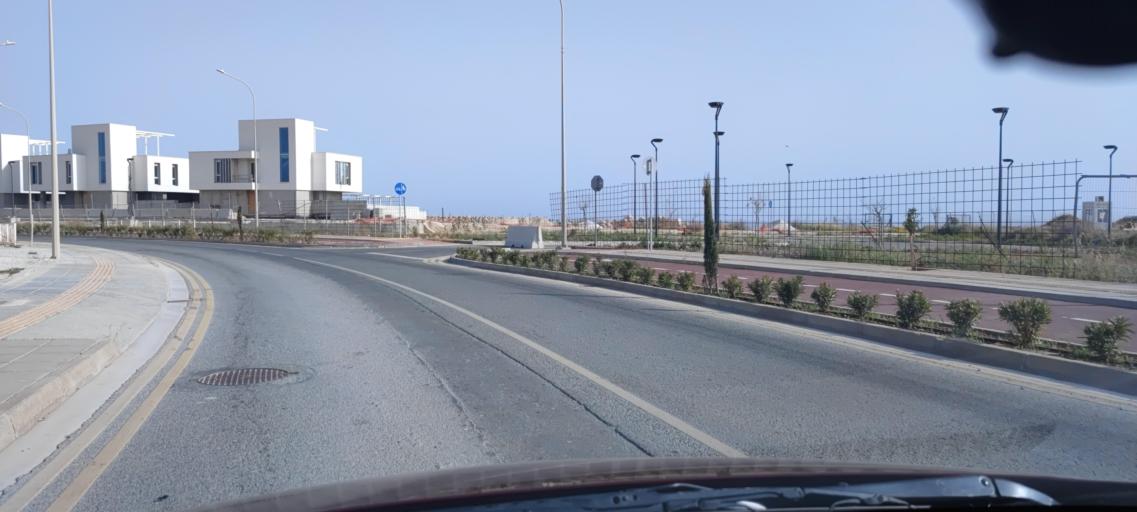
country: CY
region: Ammochostos
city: Liopetri
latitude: 34.9799
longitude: 33.9394
